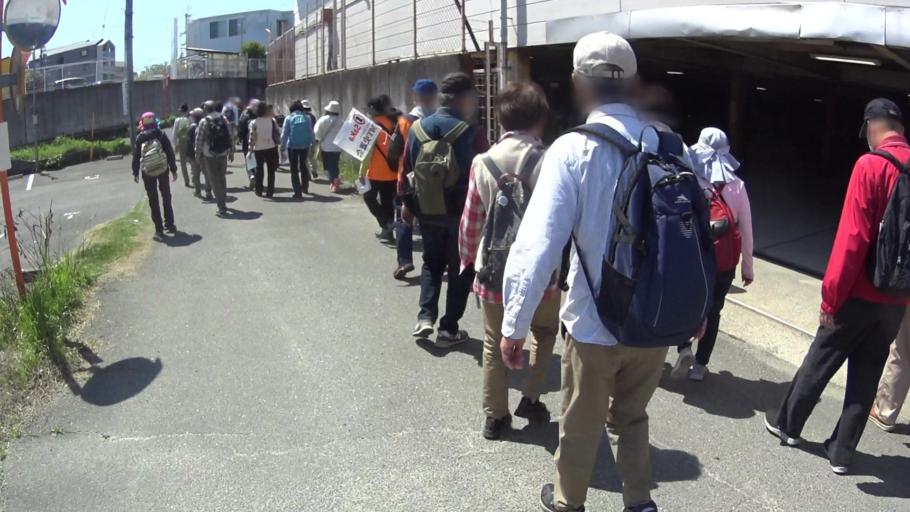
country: JP
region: Osaka
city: Kashihara
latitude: 34.5628
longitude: 135.6059
